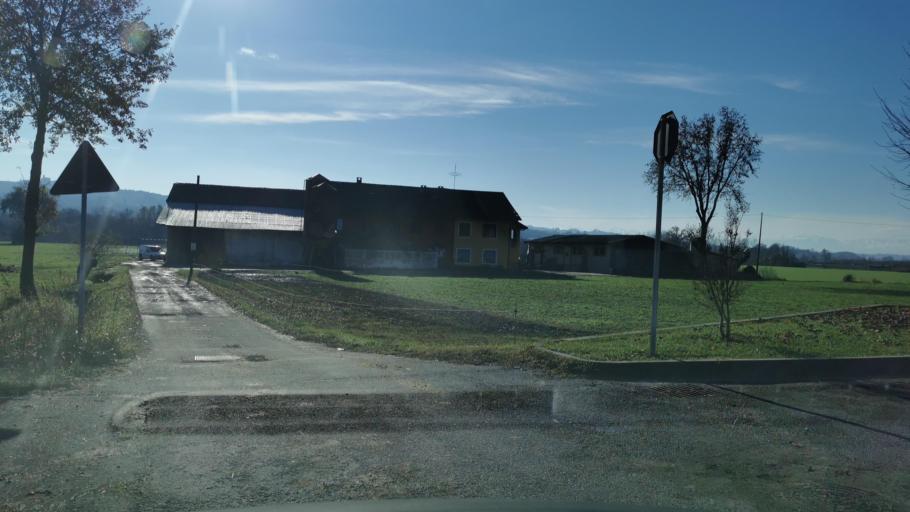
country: IT
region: Piedmont
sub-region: Provincia di Cuneo
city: Cinzano
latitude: 44.6915
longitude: 7.9160
